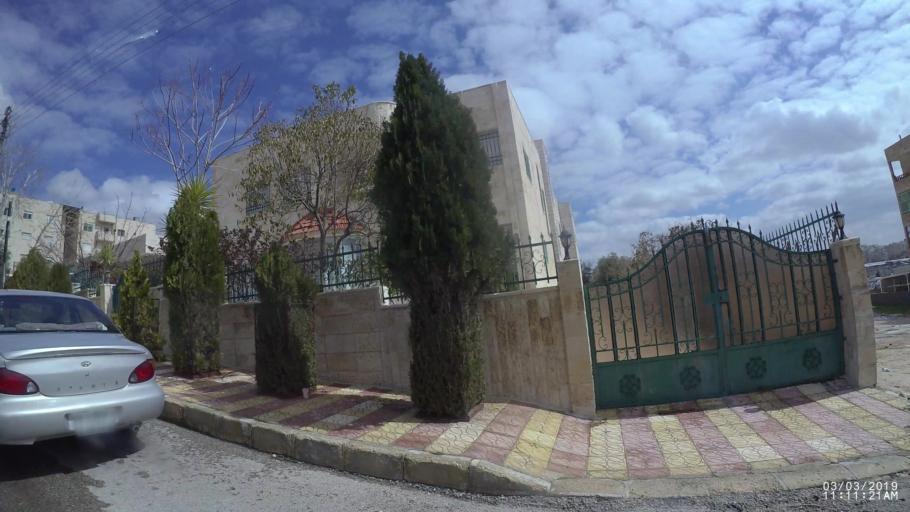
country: JO
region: Amman
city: Amman
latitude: 31.9963
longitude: 35.9160
